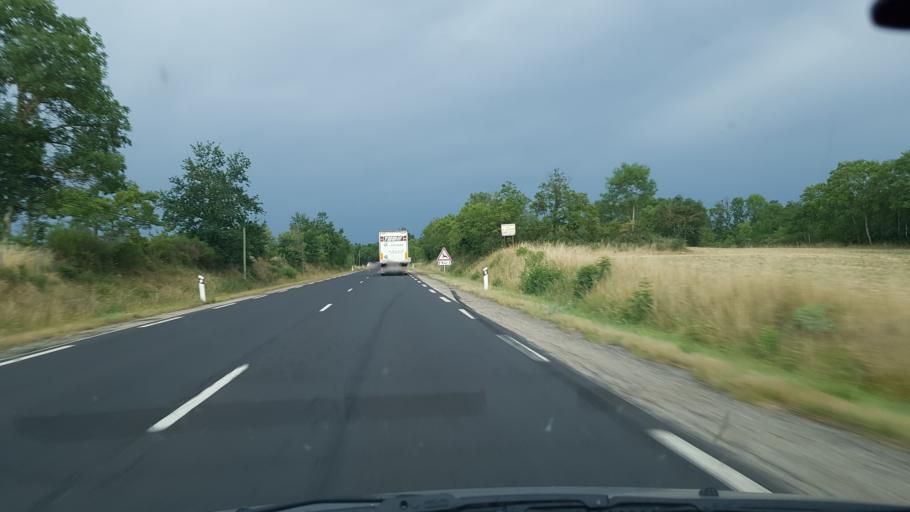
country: FR
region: Auvergne
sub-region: Departement de la Haute-Loire
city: Paulhaguet
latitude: 45.1478
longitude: 3.5505
